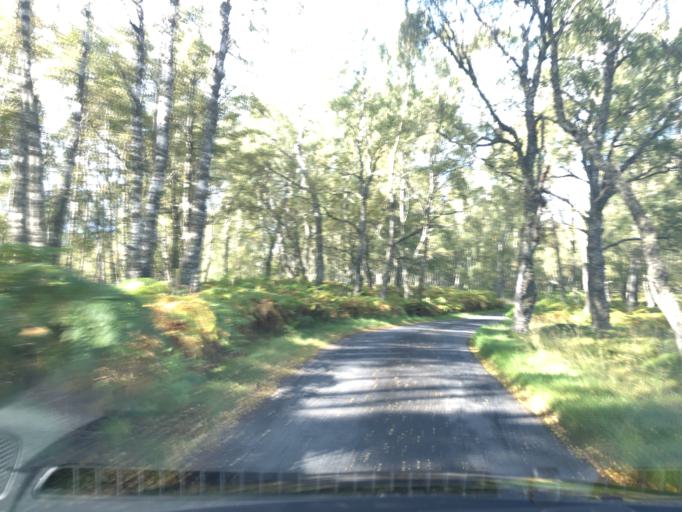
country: GB
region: Scotland
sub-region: Highland
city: Aviemore
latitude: 57.0646
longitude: -3.8993
